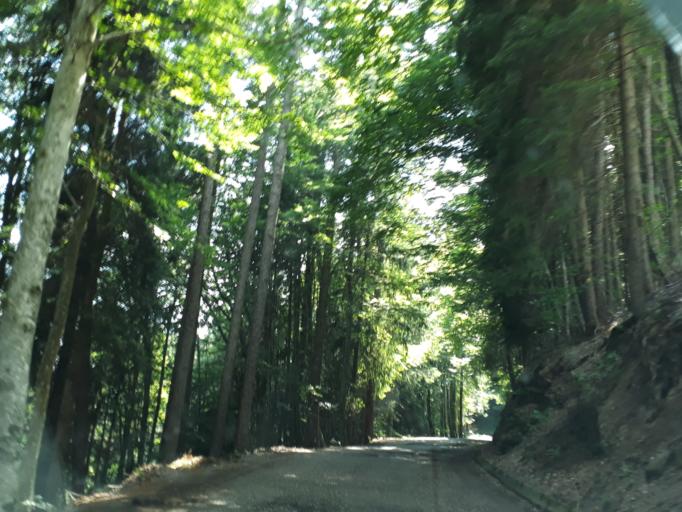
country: IT
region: Trentino-Alto Adige
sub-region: Provincia di Trento
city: Castel Condino
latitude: 45.9300
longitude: 10.5948
